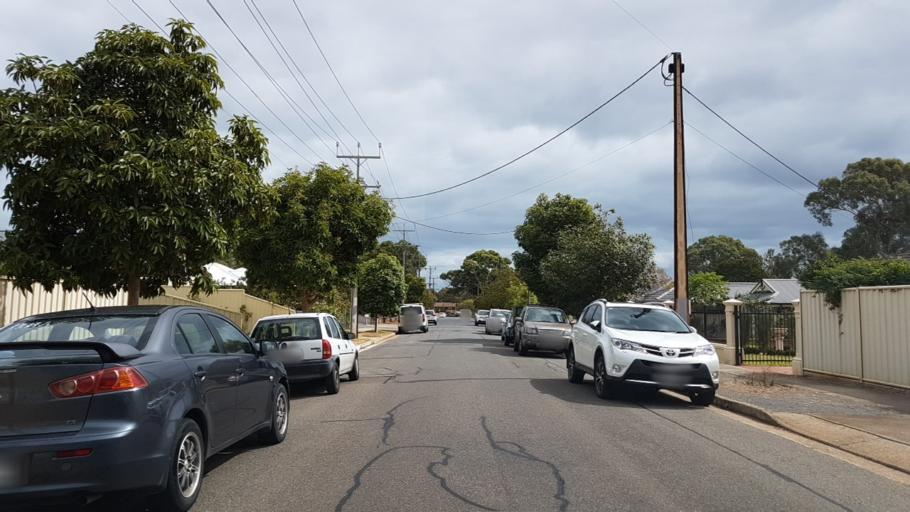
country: AU
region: South Australia
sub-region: Marion
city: Clovelly Park
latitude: -35.0035
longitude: 138.5724
